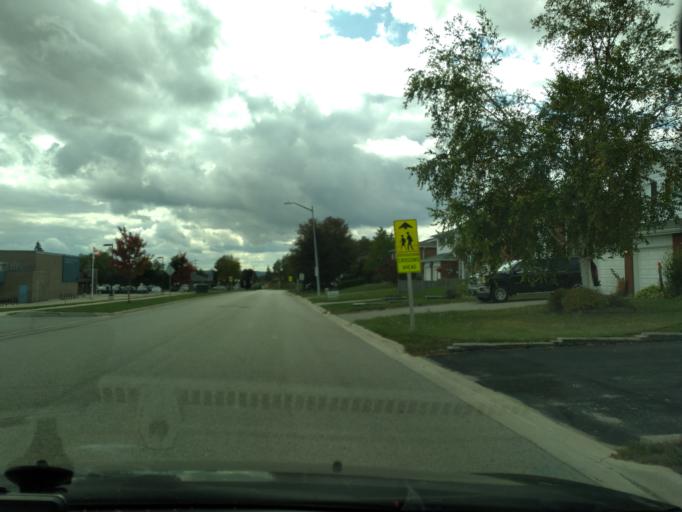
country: CA
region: Ontario
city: Bradford West Gwillimbury
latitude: 44.1190
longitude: -79.5618
